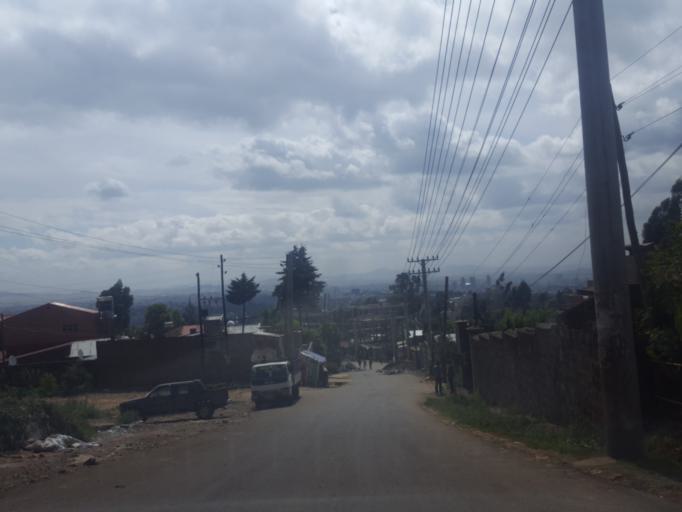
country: ET
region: Adis Abeba
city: Addis Ababa
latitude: 9.0656
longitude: 38.7418
